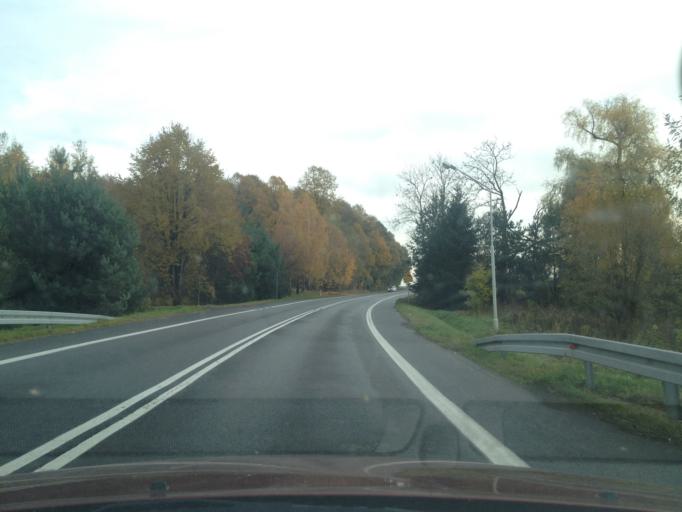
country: PL
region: Lower Silesian Voivodeship
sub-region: Powiat lubanski
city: Siekierczyn
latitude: 51.1476
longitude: 15.1791
